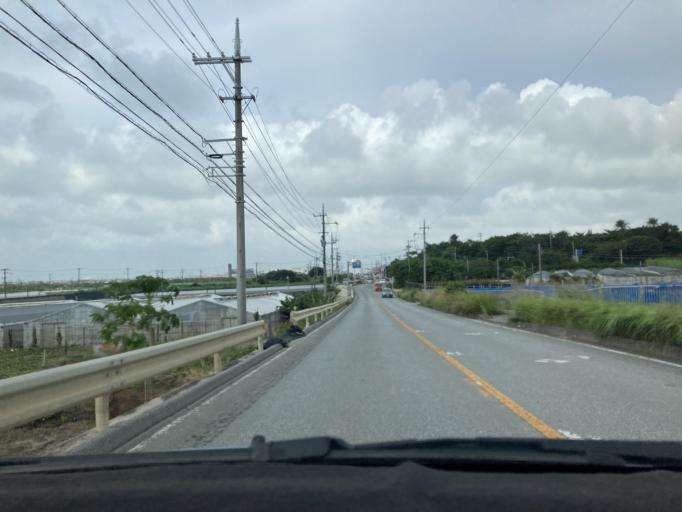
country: JP
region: Okinawa
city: Itoman
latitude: 26.1099
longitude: 127.6681
